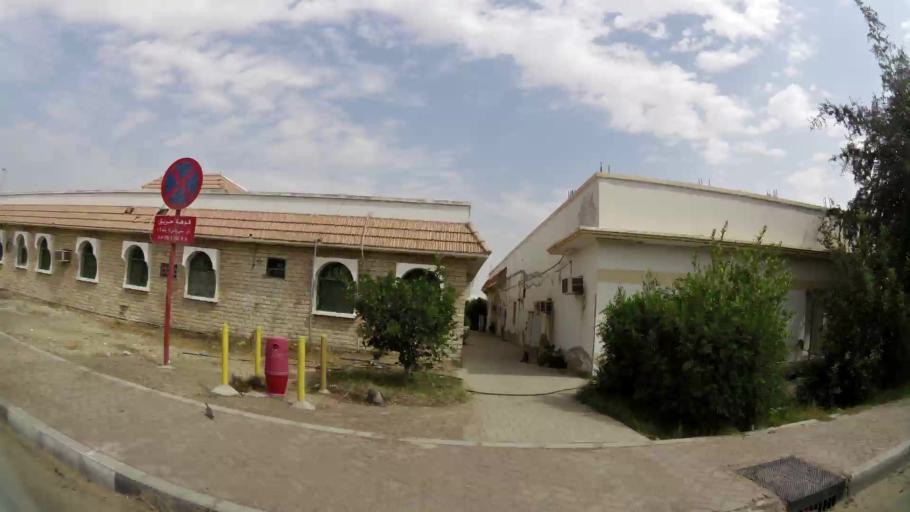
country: AE
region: Abu Dhabi
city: Abu Dhabi
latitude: 24.3012
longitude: 54.6224
